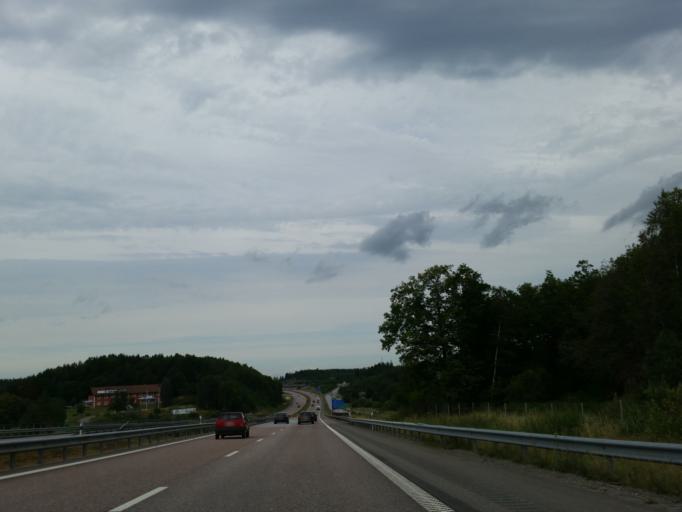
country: SE
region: Soedermanland
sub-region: Strangnas Kommun
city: Mariefred
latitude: 59.2397
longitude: 17.1804
